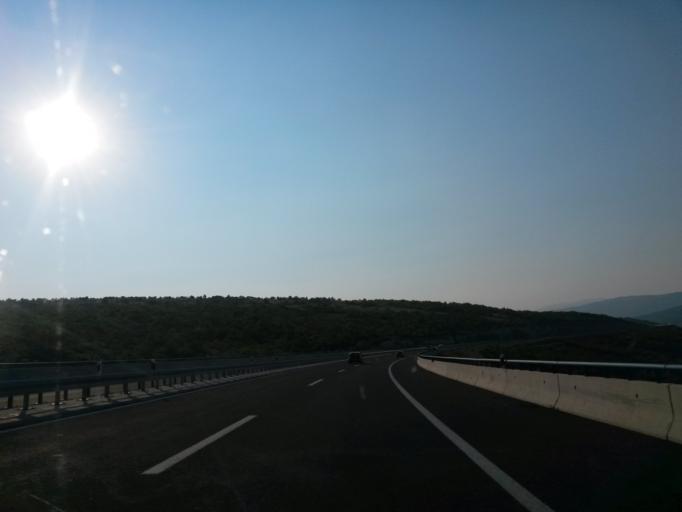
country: HR
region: Splitsko-Dalmatinska
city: Dugopolje
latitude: 43.5890
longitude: 16.6298
